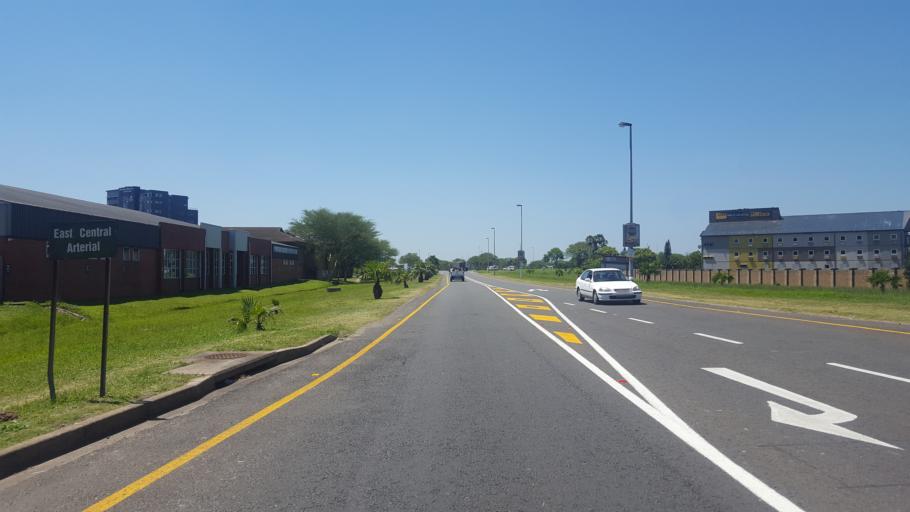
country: ZA
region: KwaZulu-Natal
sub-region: uThungulu District Municipality
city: Richards Bay
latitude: -28.7531
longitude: 32.0543
